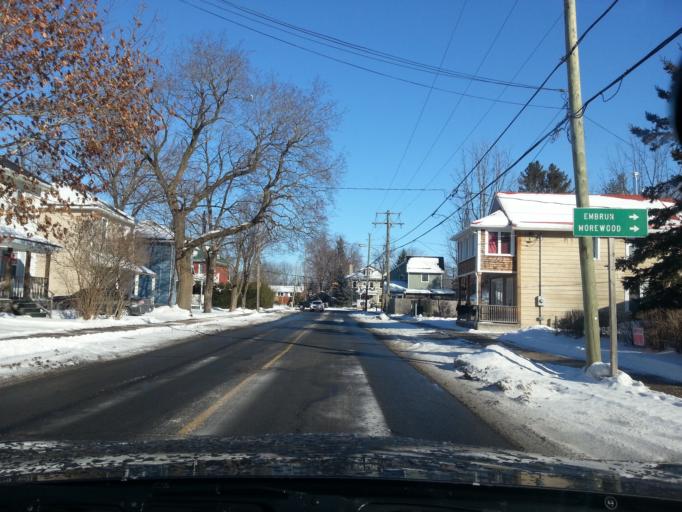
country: CA
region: Ontario
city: Bourget
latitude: 45.2589
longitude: -75.3607
